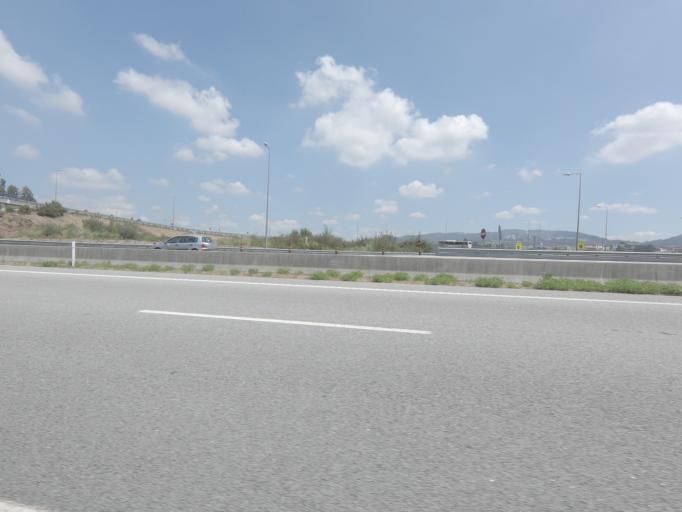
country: PT
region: Porto
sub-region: Valongo
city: Campo
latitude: 41.1795
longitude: -8.4441
